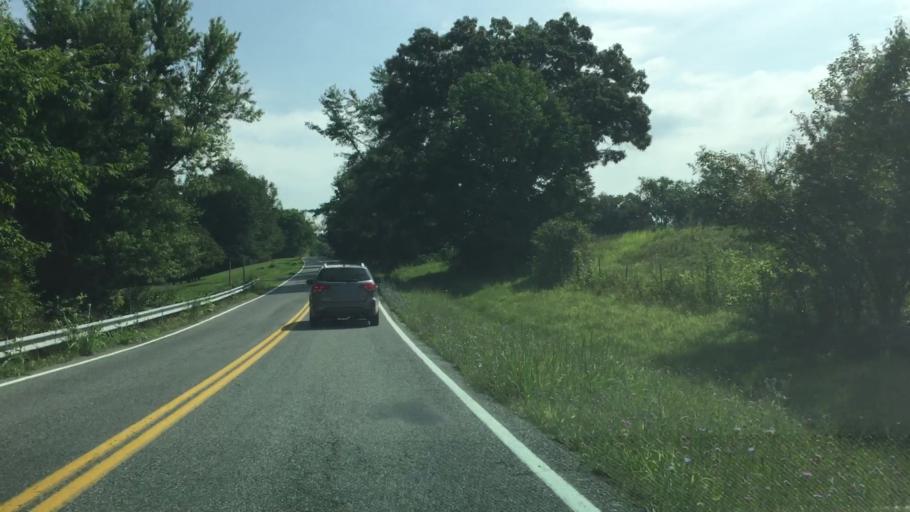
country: US
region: Virginia
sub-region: Pulaski County
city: Pulaski
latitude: 36.9802
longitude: -80.8333
